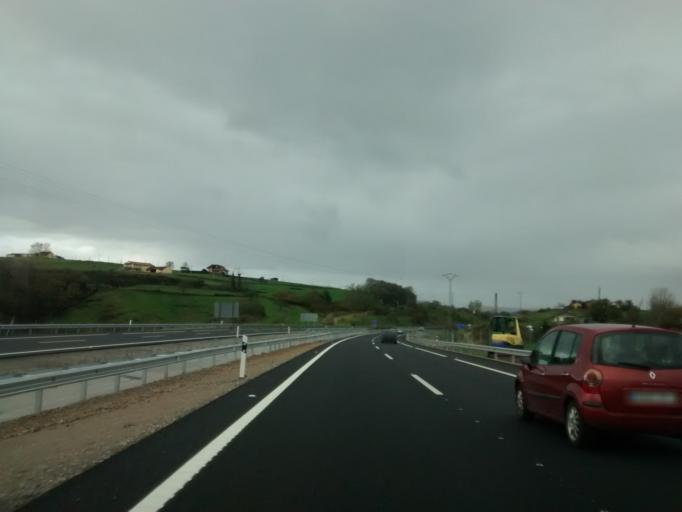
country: ES
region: Cantabria
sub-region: Provincia de Cantabria
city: Torrelavega
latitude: 43.3448
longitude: -4.0147
